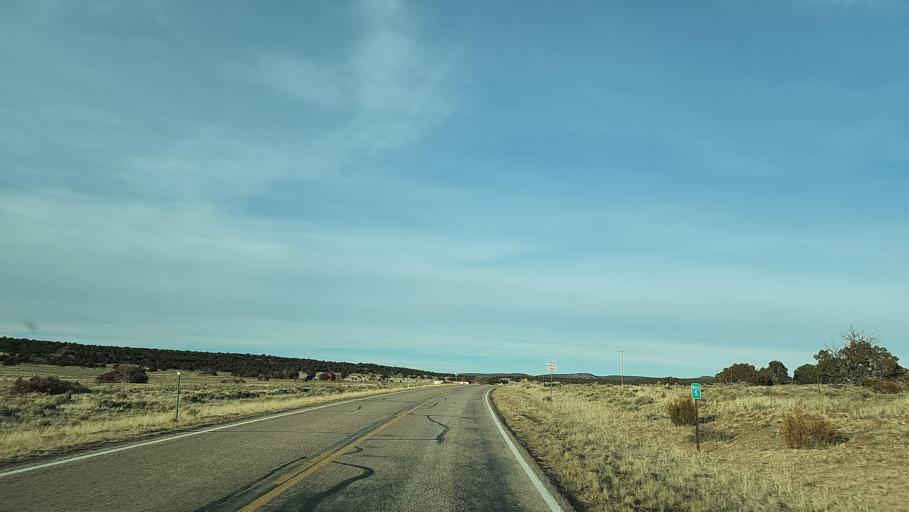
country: US
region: New Mexico
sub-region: Catron County
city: Reserve
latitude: 34.3973
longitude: -108.4443
